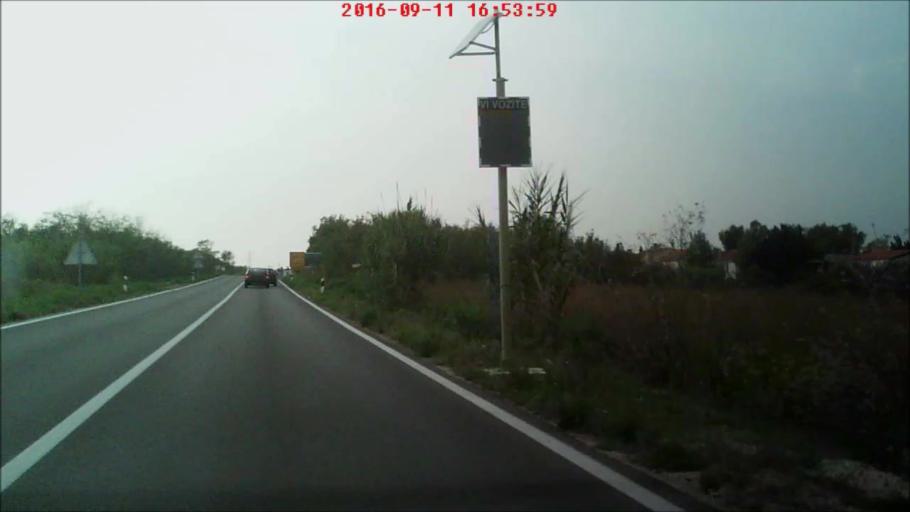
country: HR
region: Zadarska
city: Nin
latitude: 44.2518
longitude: 15.1612
